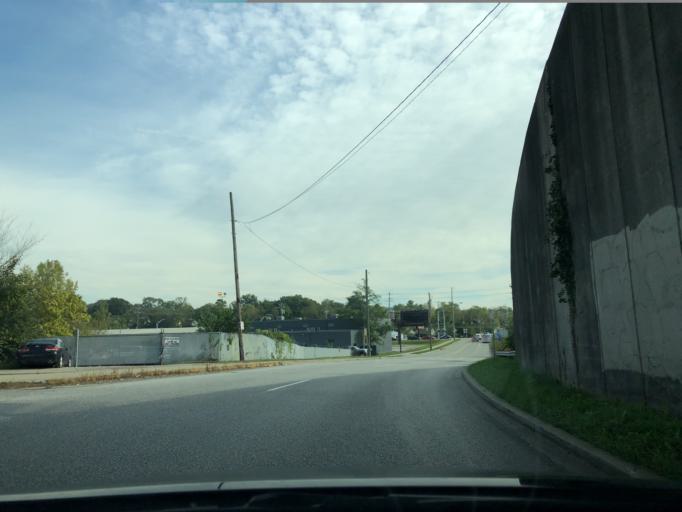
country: US
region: Ohio
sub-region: Hamilton County
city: Golf Manor
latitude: 39.1658
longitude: -84.4228
